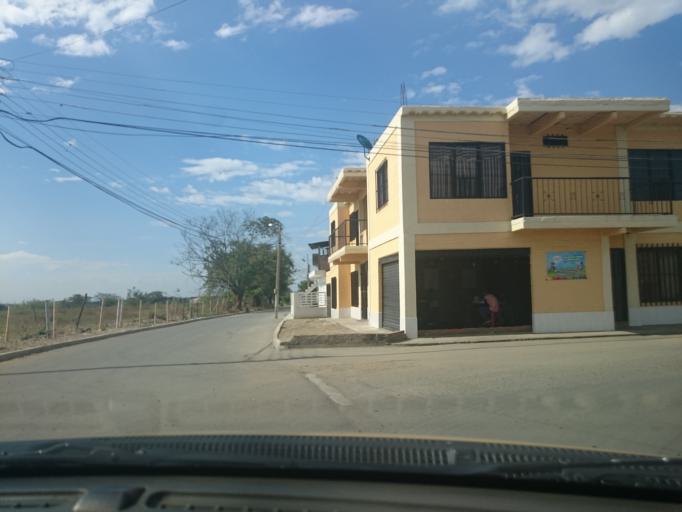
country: CO
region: Cauca
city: Santander de Quilichao
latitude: 3.0167
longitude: -76.4851
